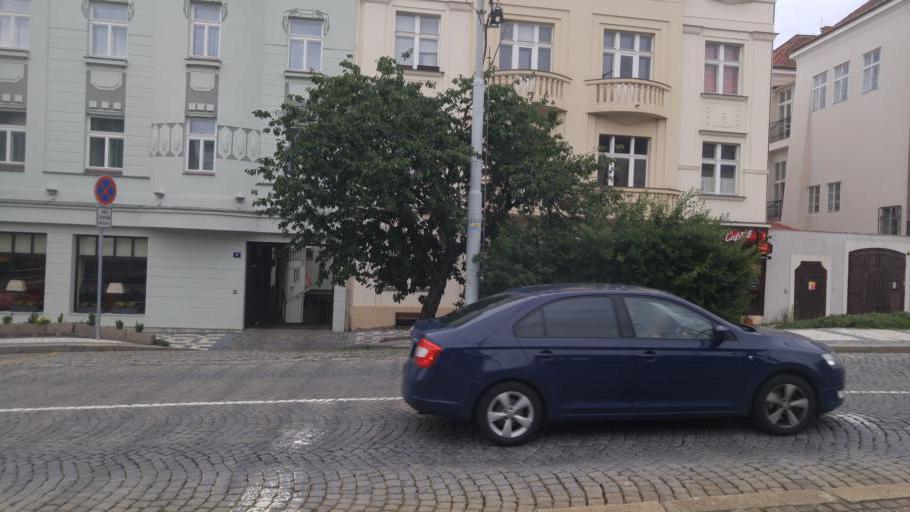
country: CZ
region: Praha
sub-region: Praha 1
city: Mala Strana
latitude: 50.0881
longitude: 14.3881
